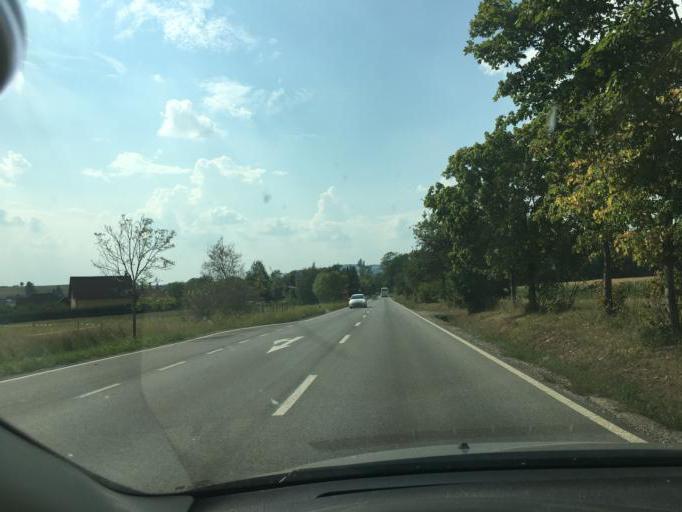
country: CZ
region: Kralovehradecky
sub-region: Okres Trutnov
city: Vrchlabi
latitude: 50.6175
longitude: 15.6684
